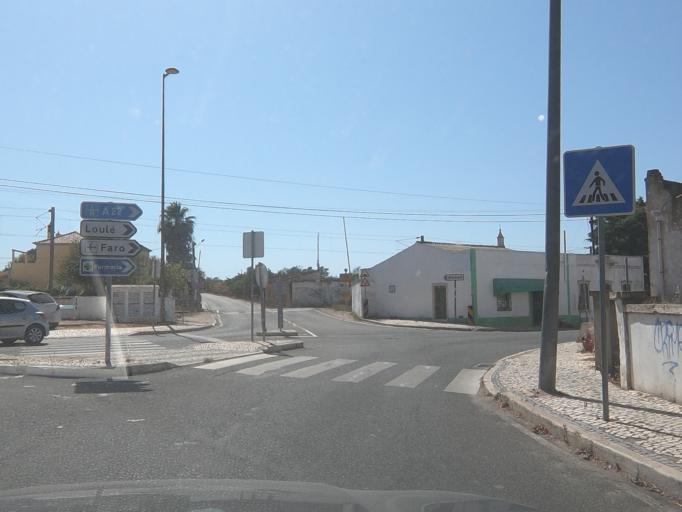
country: PT
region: Faro
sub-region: Faro
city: Santa Barbara de Nexe
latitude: 37.0865
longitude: -7.9900
